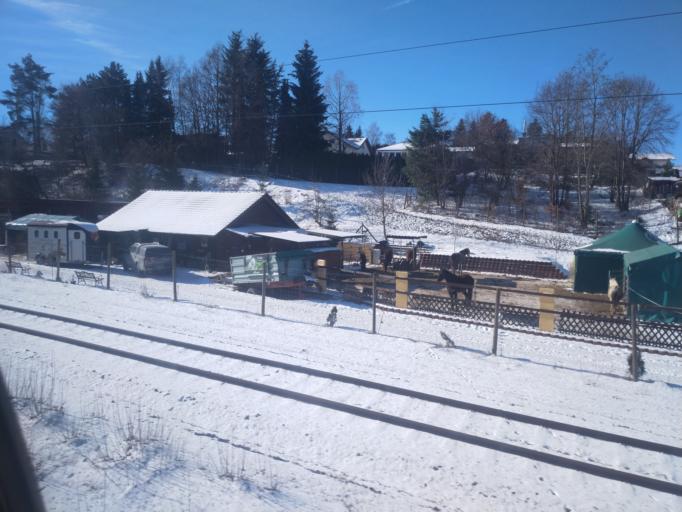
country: DE
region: Baden-Wuerttemberg
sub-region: Freiburg Region
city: Aldingen
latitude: 48.0926
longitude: 8.7164
